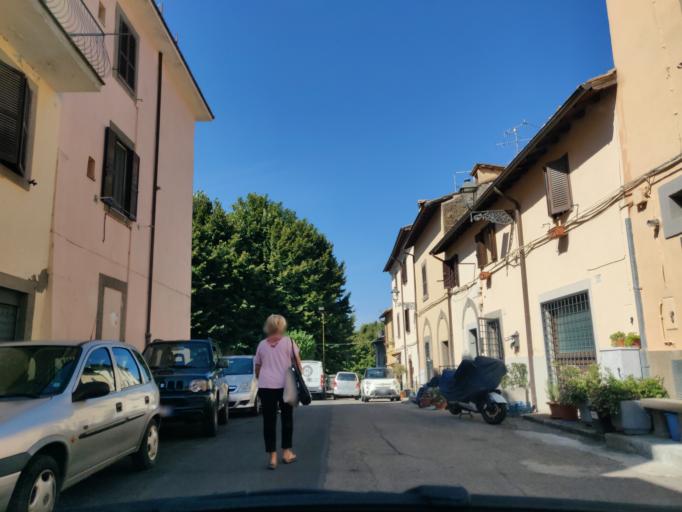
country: IT
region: Latium
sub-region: Provincia di Viterbo
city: Viterbo
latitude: 42.4302
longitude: 12.1284
